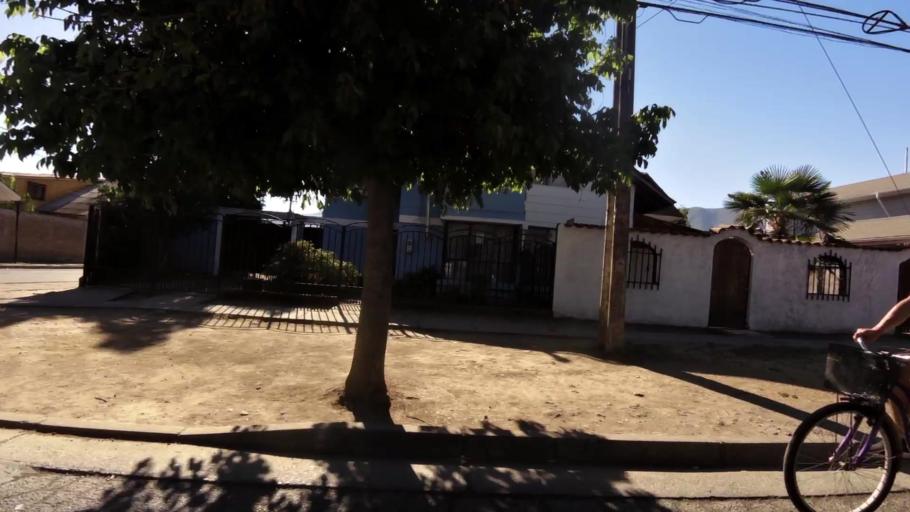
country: CL
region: O'Higgins
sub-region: Provincia de Colchagua
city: Chimbarongo
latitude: -34.5764
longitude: -70.9990
